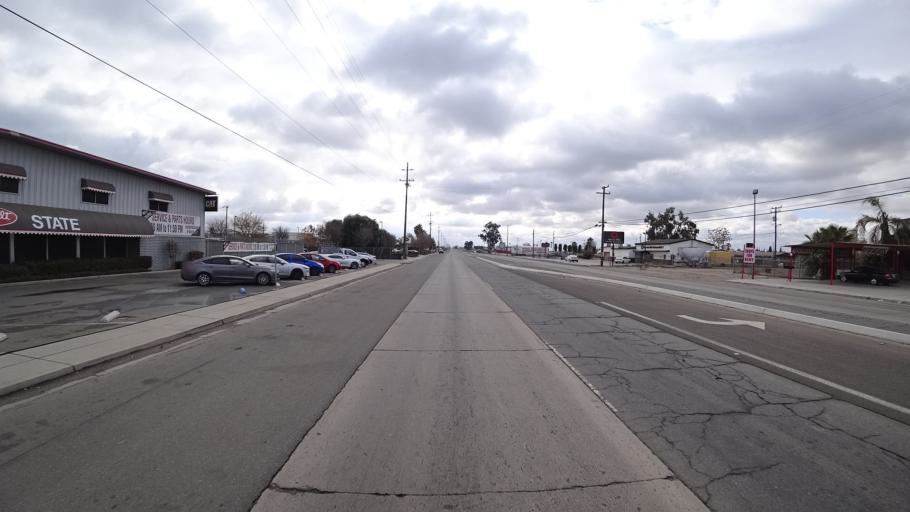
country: US
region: California
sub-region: Kern County
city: Bakersfield
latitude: 35.3371
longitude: -119.0030
